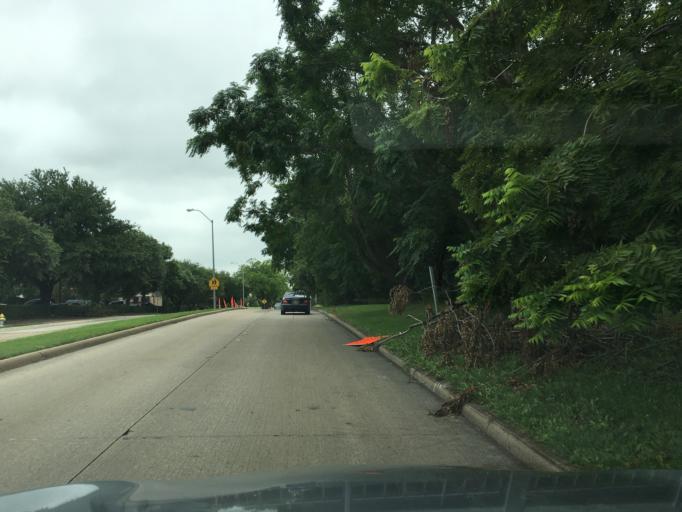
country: US
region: Texas
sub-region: Dallas County
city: Richardson
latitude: 32.9359
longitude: -96.7376
